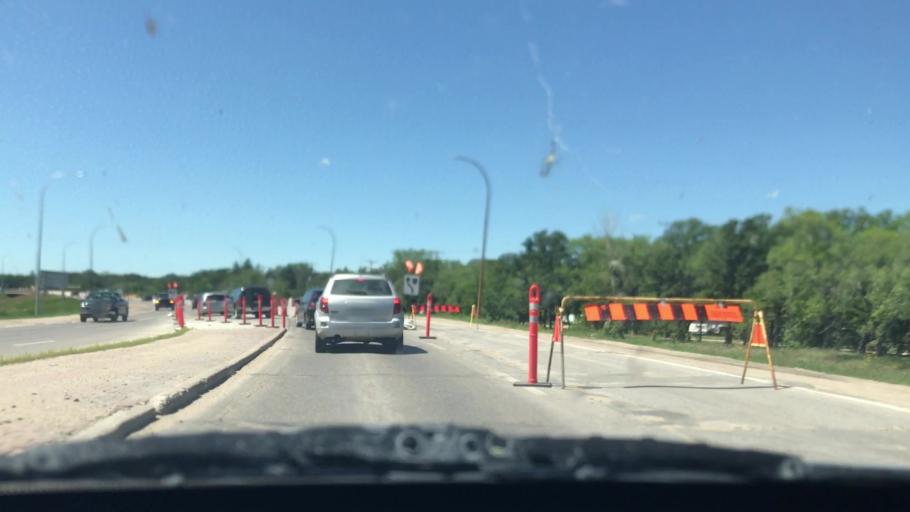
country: CA
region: Manitoba
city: Winnipeg
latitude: 49.8574
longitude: -97.0906
